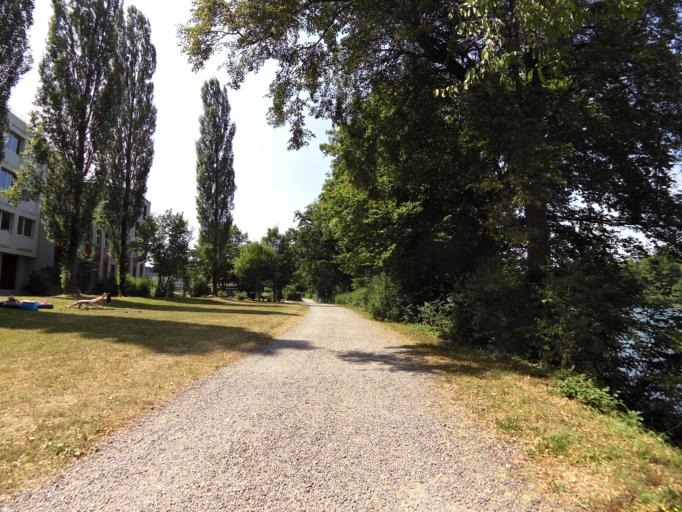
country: CH
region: Aargau
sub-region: Bezirk Baden
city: Neuenhof
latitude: 47.4564
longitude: 8.3271
